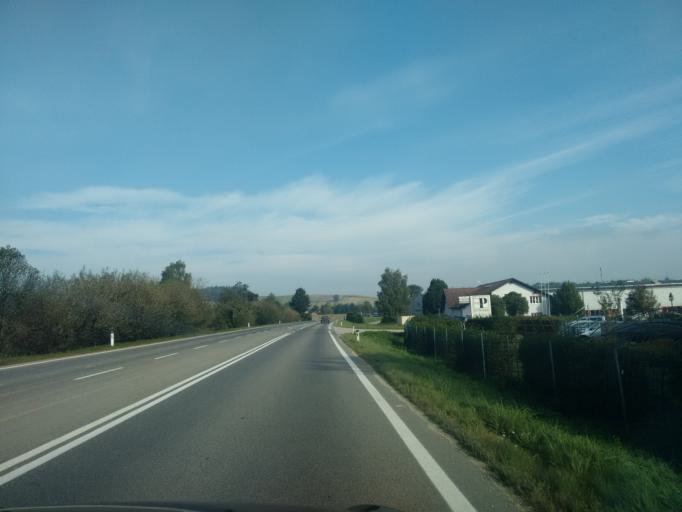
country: AT
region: Upper Austria
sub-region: Politischer Bezirk Grieskirchen
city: Grieskirchen
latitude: 48.2427
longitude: 13.7665
